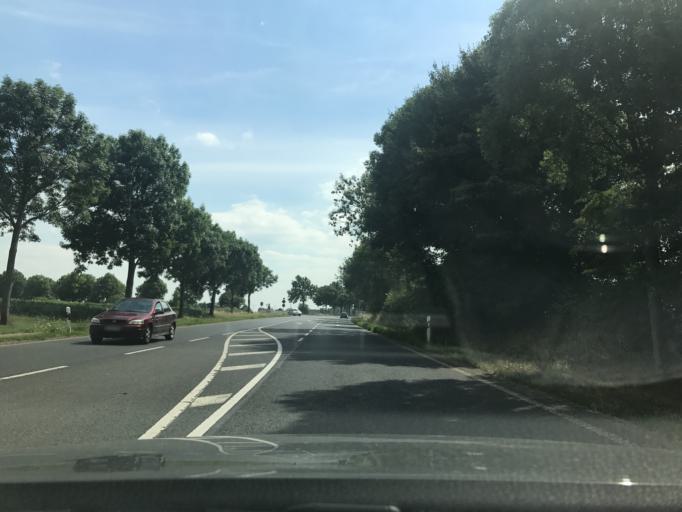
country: DE
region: North Rhine-Westphalia
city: Tonisvorst
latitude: 51.3966
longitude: 6.4964
